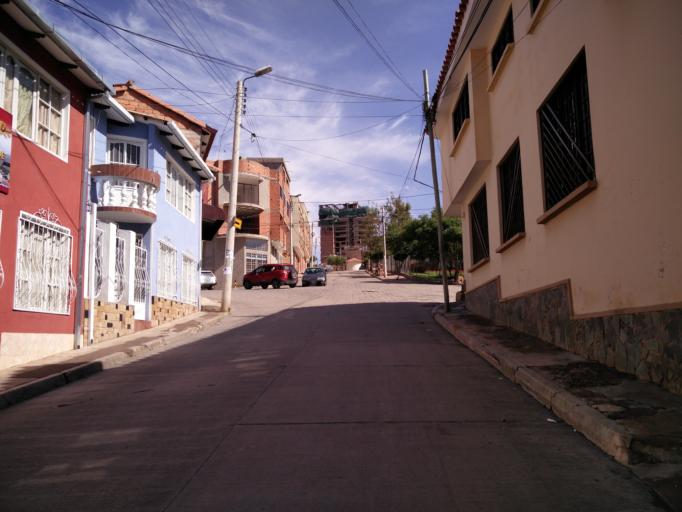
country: BO
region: Chuquisaca
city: Sucre
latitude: -19.0381
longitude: -65.2459
